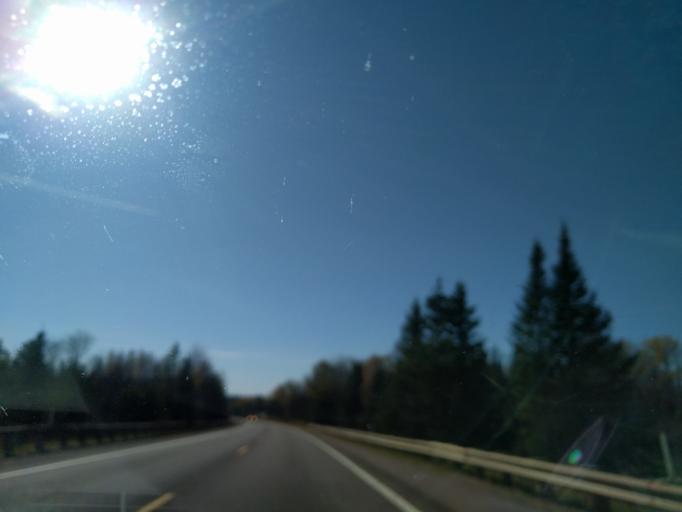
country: US
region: Michigan
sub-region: Marquette County
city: West Ishpeming
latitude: 46.4175
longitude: -87.9895
